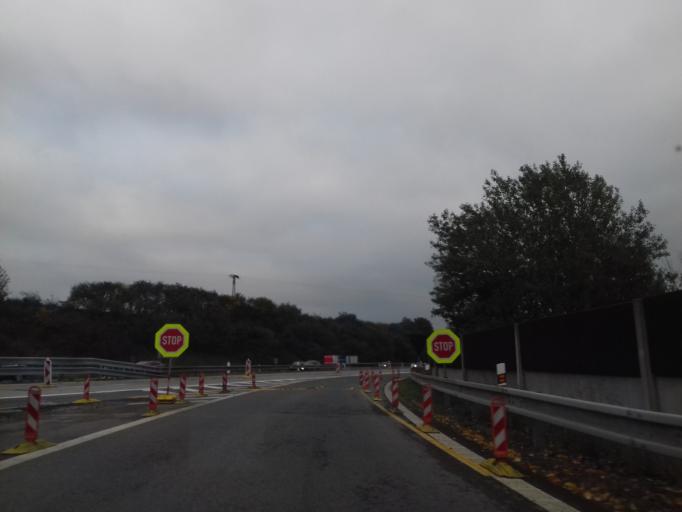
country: CZ
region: Central Bohemia
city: Divisov
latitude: 49.8383
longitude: 14.8300
